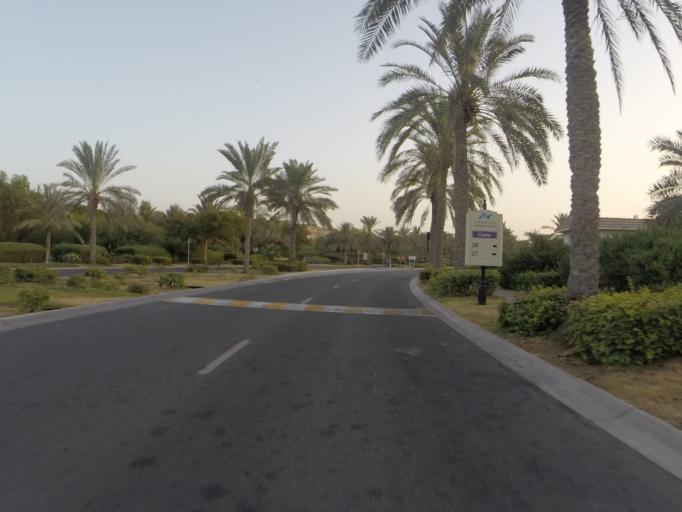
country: AE
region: Dubai
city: Dubai
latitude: 25.0508
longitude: 55.1648
